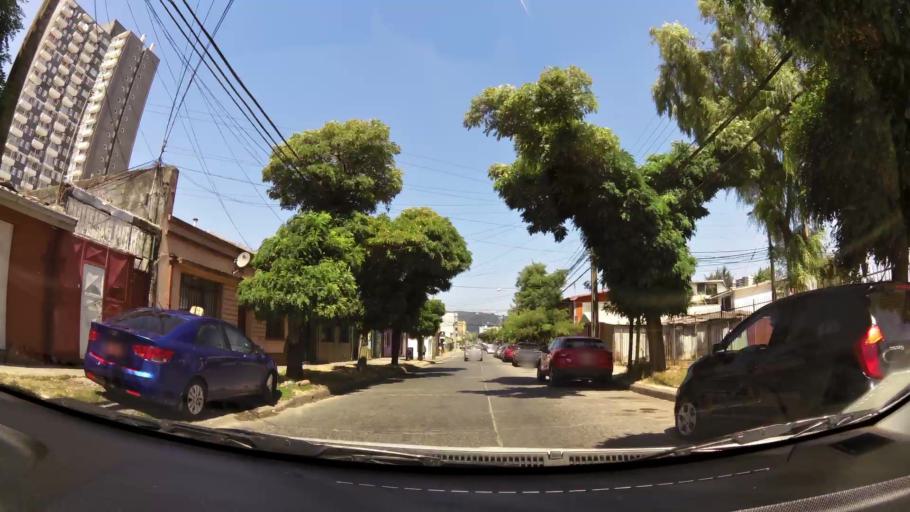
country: CL
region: Biobio
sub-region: Provincia de Concepcion
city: Concepcion
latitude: -36.8177
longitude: -73.0554
